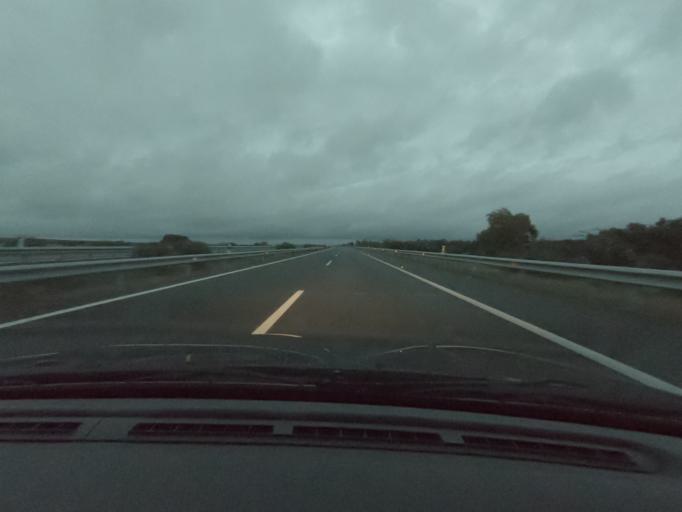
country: ES
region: Extremadura
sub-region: Provincia de Caceres
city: Casas de Don Antonio
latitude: 39.2429
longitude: -6.3049
